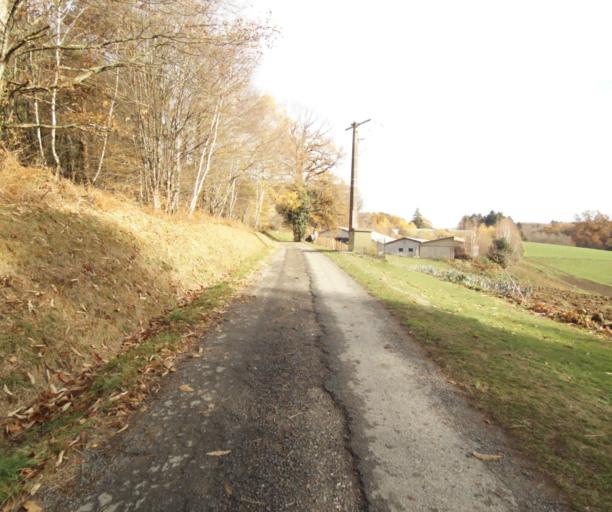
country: FR
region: Limousin
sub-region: Departement de la Correze
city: Cornil
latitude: 45.1944
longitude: 1.7236
